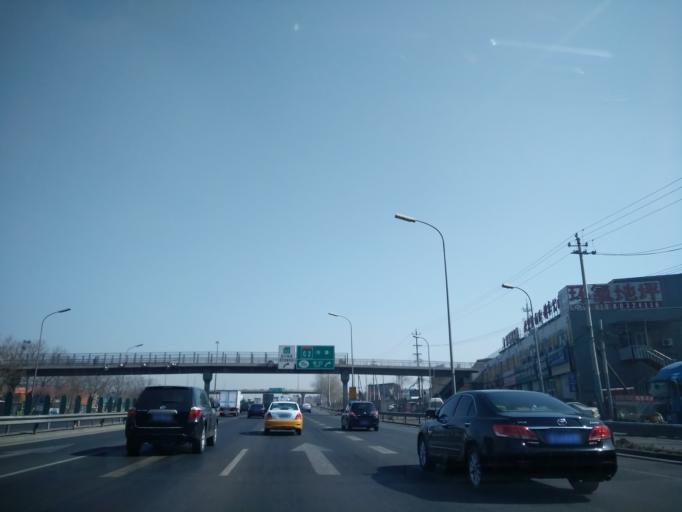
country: CN
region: Beijing
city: Jiugong
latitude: 39.8160
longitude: 116.4925
